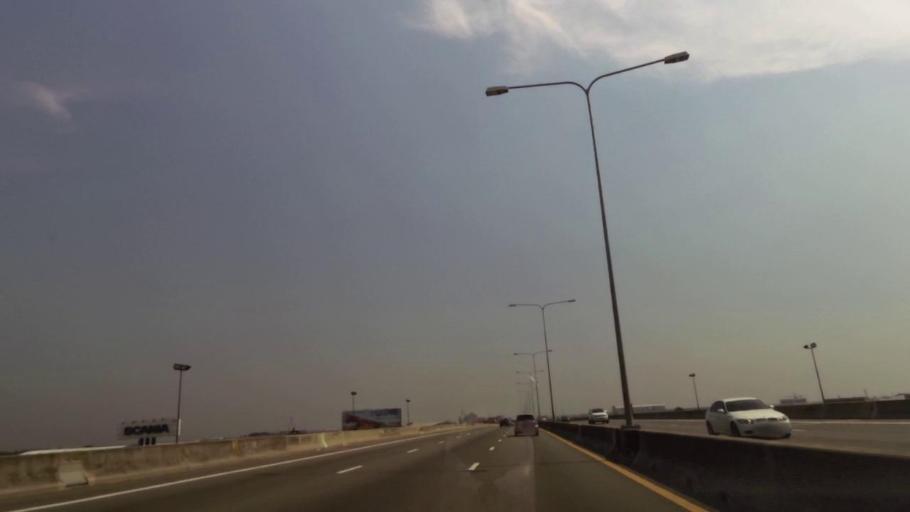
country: TH
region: Samut Prakan
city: Bang Bo District
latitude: 13.6080
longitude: 100.7671
